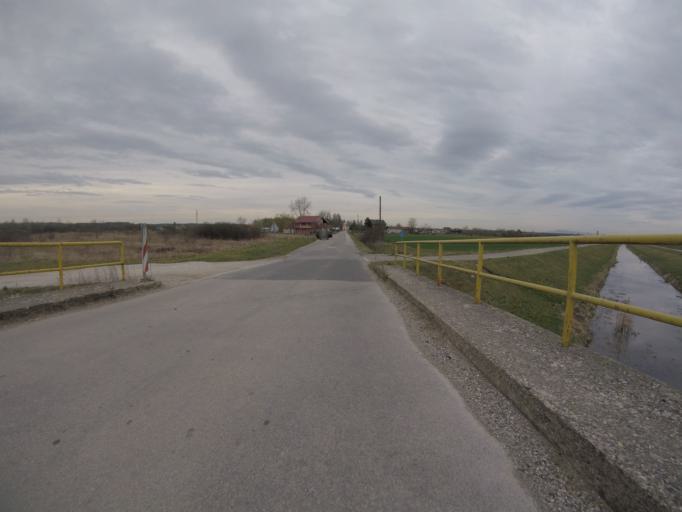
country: HR
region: Zagrebacka
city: Lukavec
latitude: 45.7051
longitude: 16.0080
